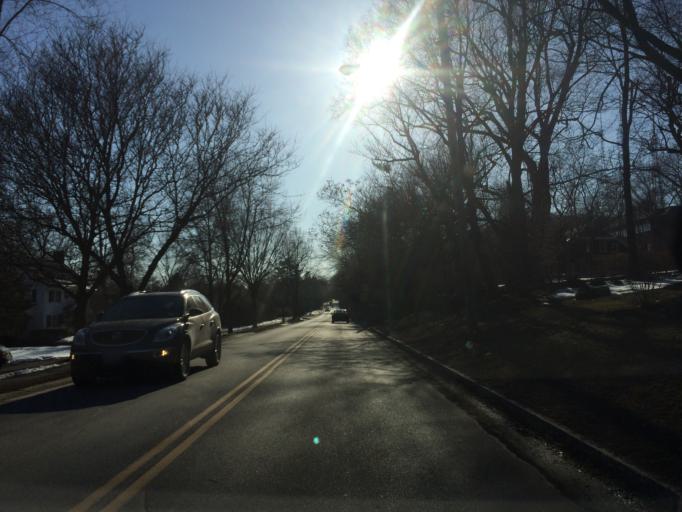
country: US
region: New York
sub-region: Monroe County
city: Brighton
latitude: 43.1354
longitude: -77.5780
